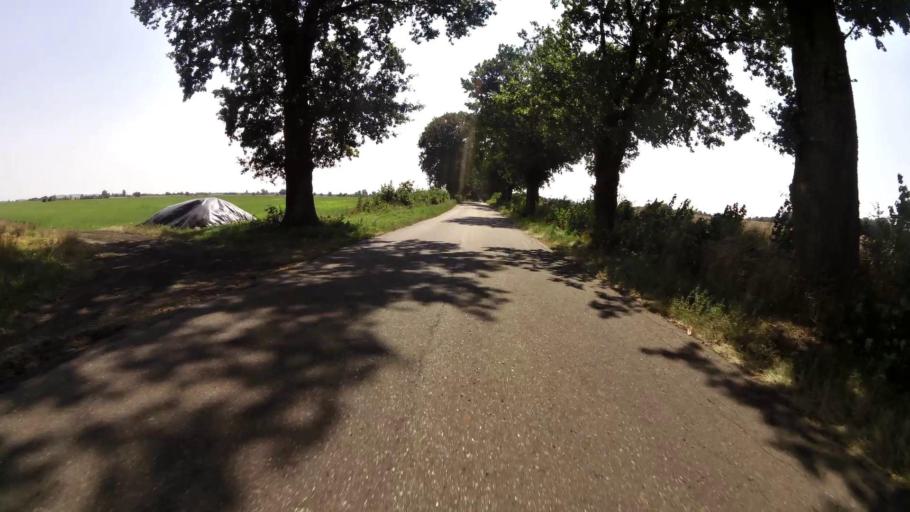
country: PL
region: West Pomeranian Voivodeship
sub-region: Powiat walecki
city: Walcz
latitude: 53.2207
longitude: 16.5007
